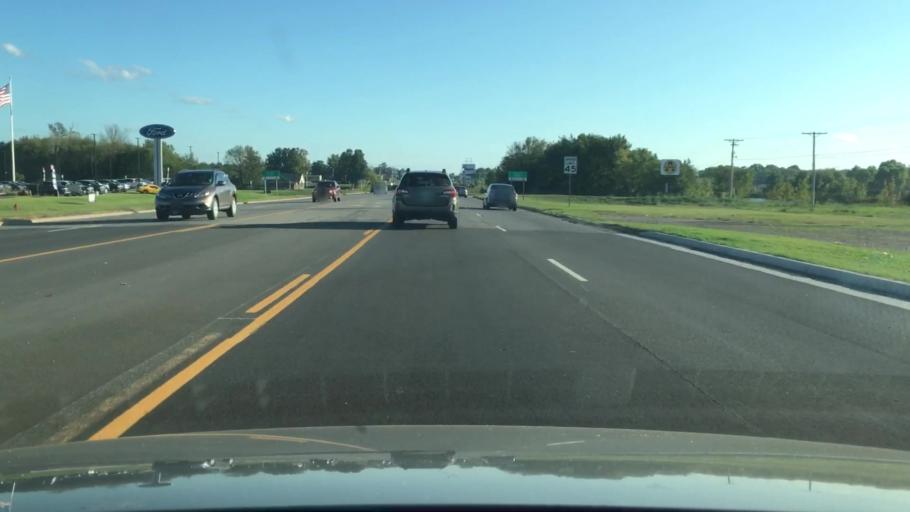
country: US
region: Oklahoma
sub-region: Cherokee County
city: Park Hill
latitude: 35.8755
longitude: -94.9763
